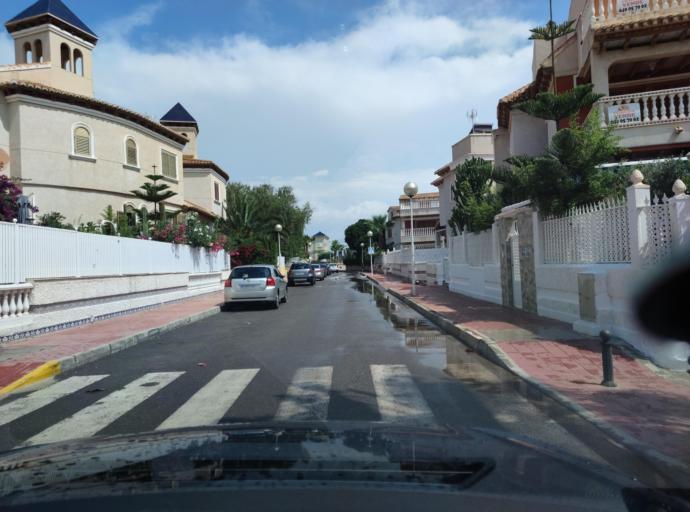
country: ES
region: Valencia
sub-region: Provincia de Alicante
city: Guardamar del Segura
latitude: 38.0643
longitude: -0.6526
